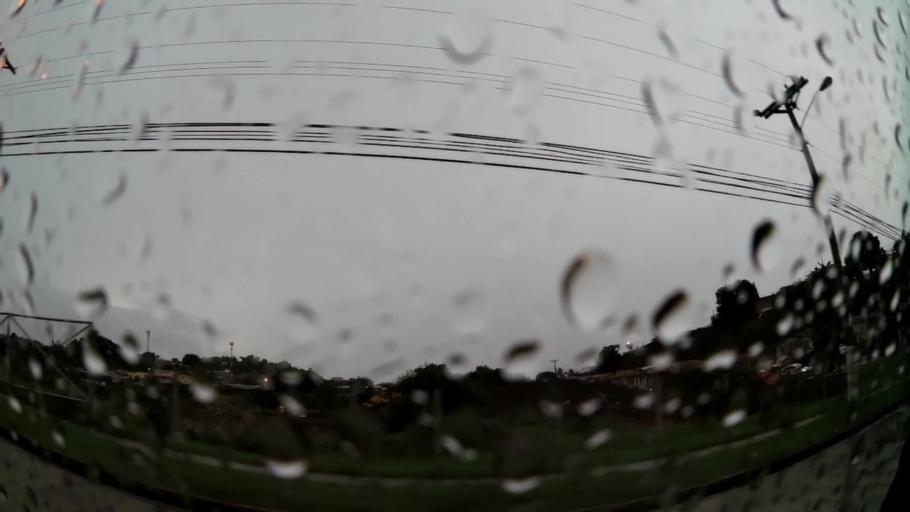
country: PA
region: Panama
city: San Miguelito
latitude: 9.0532
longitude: -79.4746
